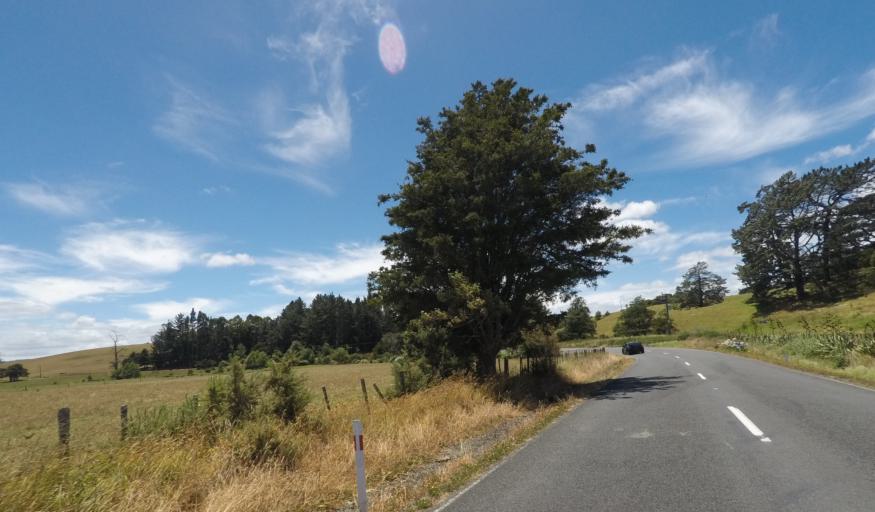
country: NZ
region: Northland
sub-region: Whangarei
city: Whangarei
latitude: -35.5474
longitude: 174.3040
